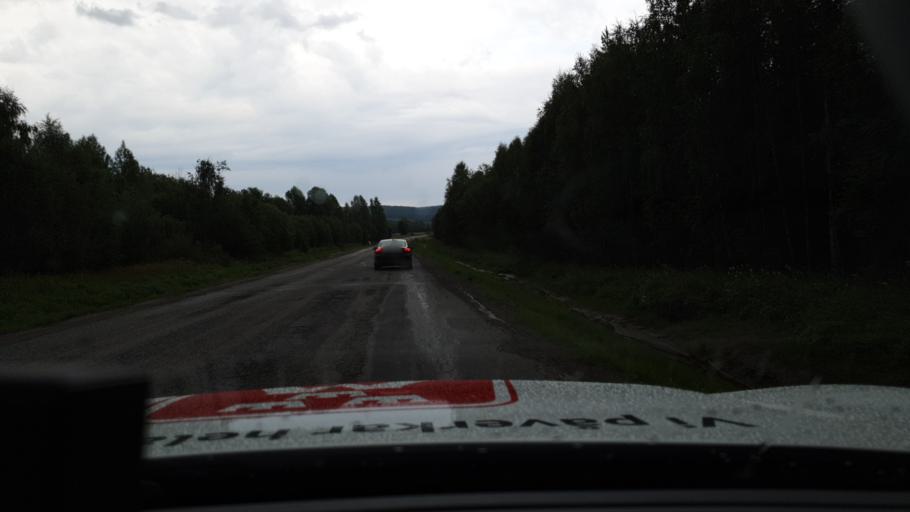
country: SE
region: Norrbotten
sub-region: Bodens Kommun
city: Boden
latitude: 65.8503
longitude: 21.5487
